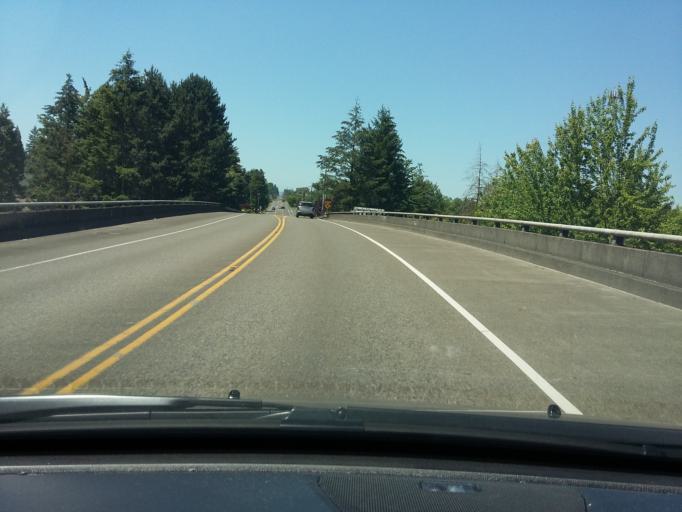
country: US
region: Washington
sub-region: Clark County
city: Five Corners
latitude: 45.6789
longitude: -122.5866
